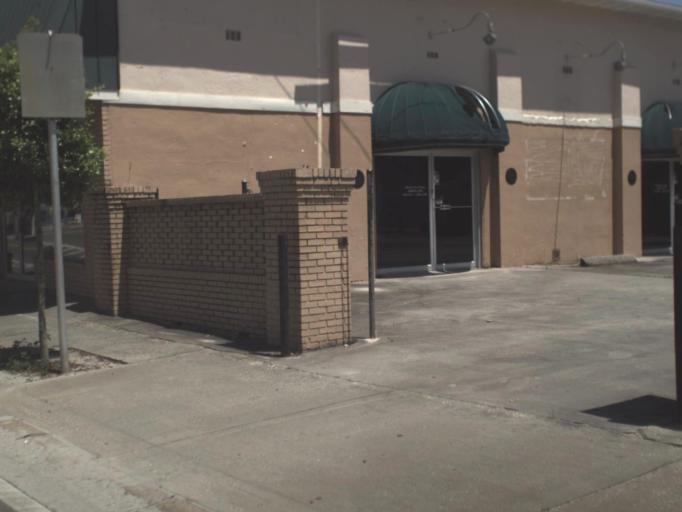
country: US
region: Florida
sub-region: Baker County
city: Macclenny
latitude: 30.2822
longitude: -82.1234
